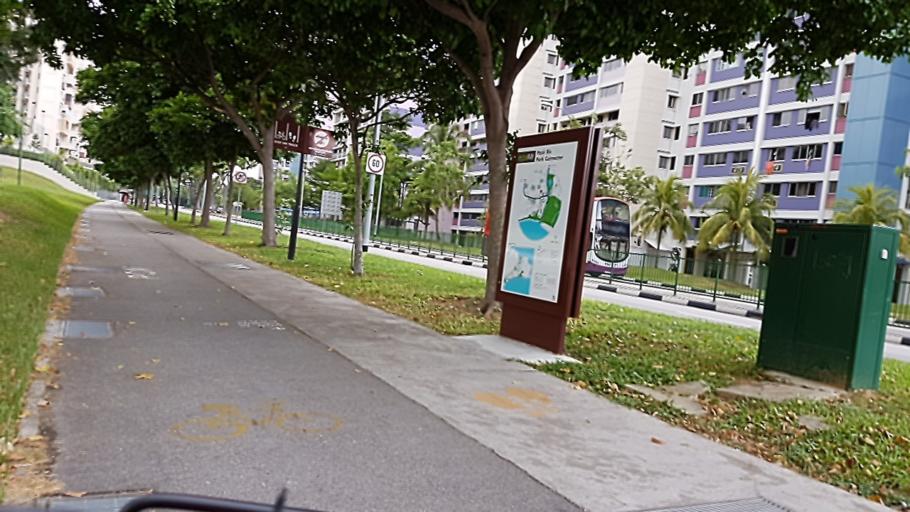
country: MY
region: Johor
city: Kampung Pasir Gudang Baru
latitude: 1.3757
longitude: 103.9563
